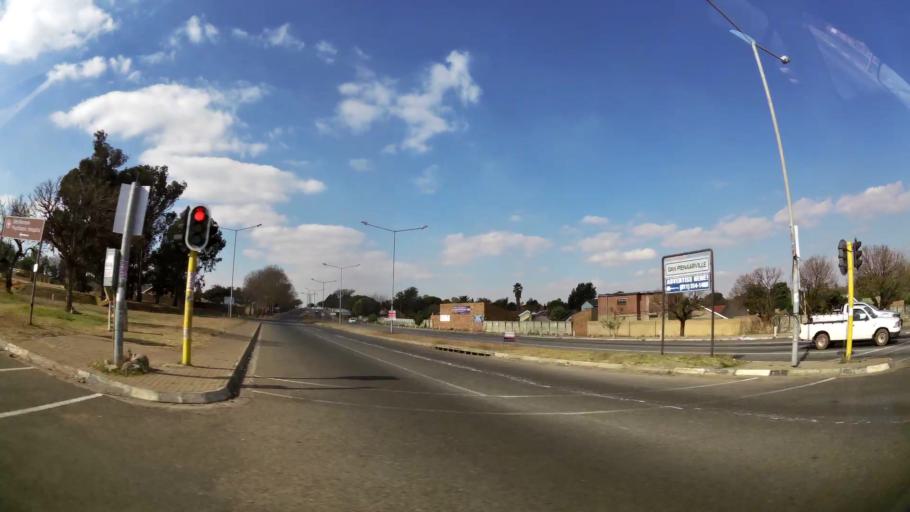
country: ZA
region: Gauteng
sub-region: West Rand District Municipality
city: Krugersdorp
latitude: -26.0814
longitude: 27.7598
